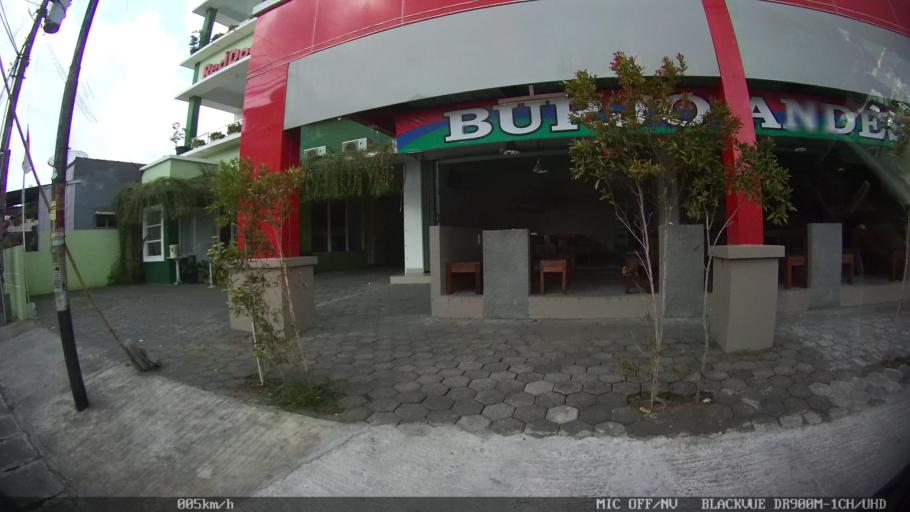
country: ID
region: Daerah Istimewa Yogyakarta
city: Gamping Lor
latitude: -7.8089
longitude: 110.3279
